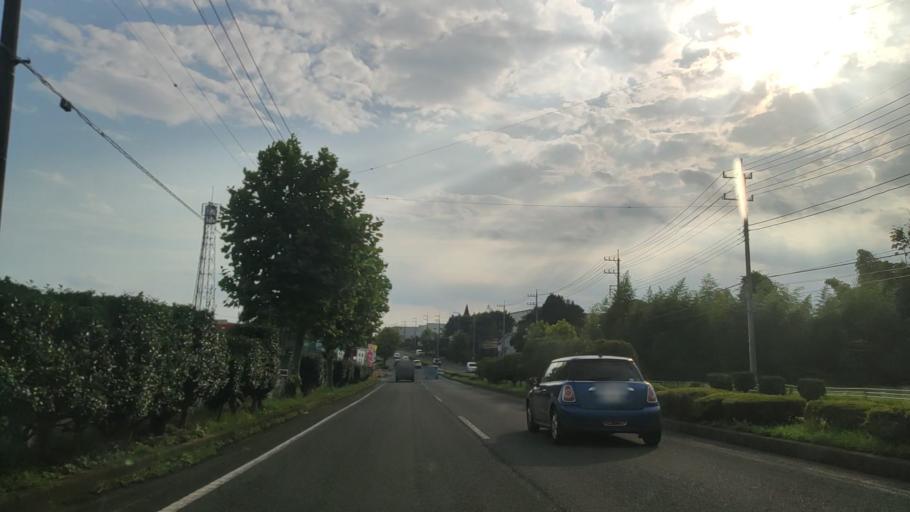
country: JP
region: Tochigi
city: Utsunomiya-shi
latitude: 36.5408
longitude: 139.8145
